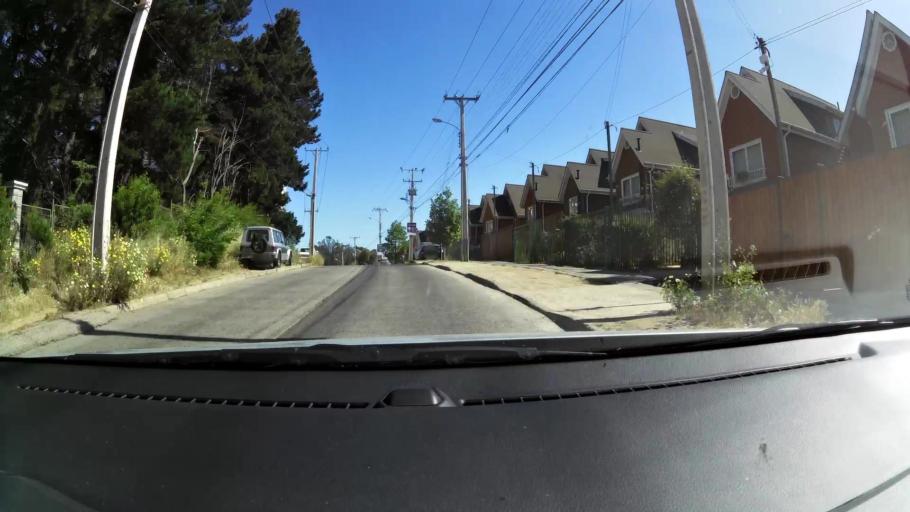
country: CL
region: Valparaiso
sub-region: Provincia de Valparaiso
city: Valparaiso
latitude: -33.0613
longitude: -71.5864
